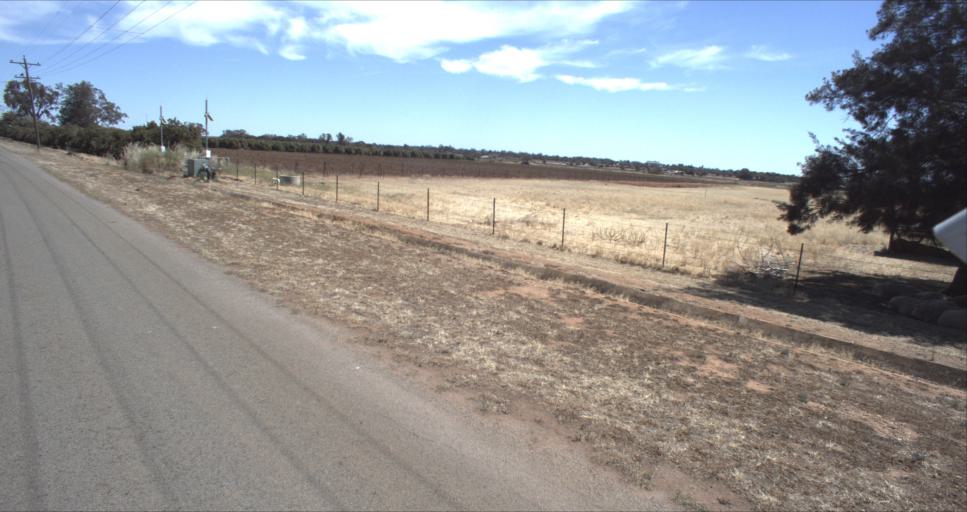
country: AU
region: New South Wales
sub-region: Leeton
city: Leeton
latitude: -34.6014
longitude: 146.4349
